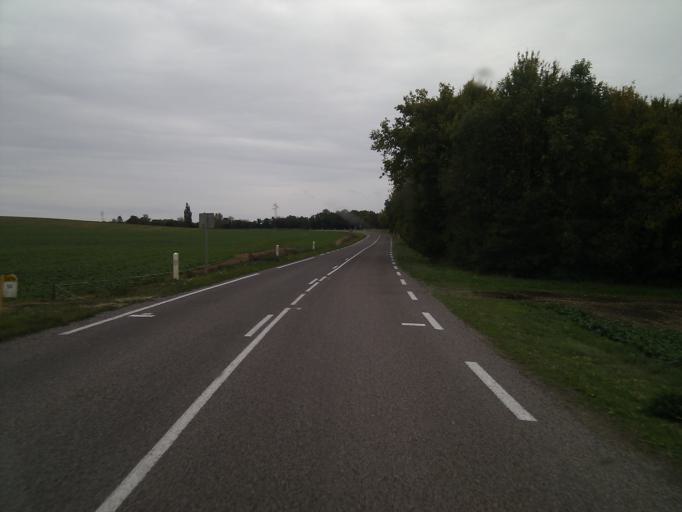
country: FR
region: Champagne-Ardenne
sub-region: Departement de la Haute-Marne
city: Doulaincourt-Saucourt
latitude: 48.2609
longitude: 5.3556
